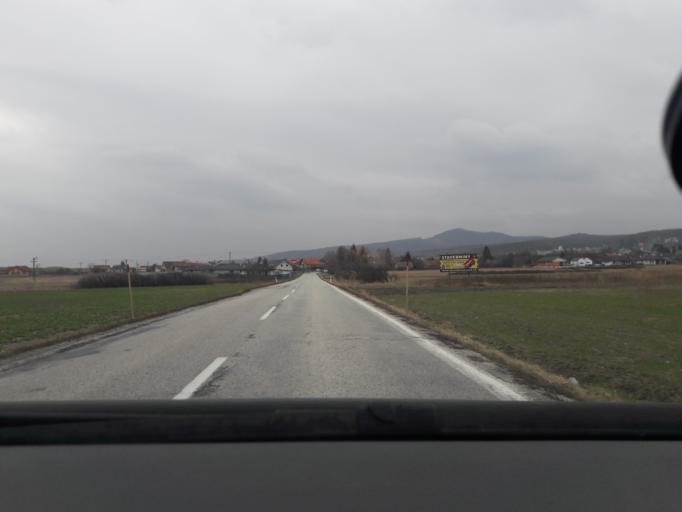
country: SK
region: Bratislavsky
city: Modra
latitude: 48.4029
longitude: 17.3718
